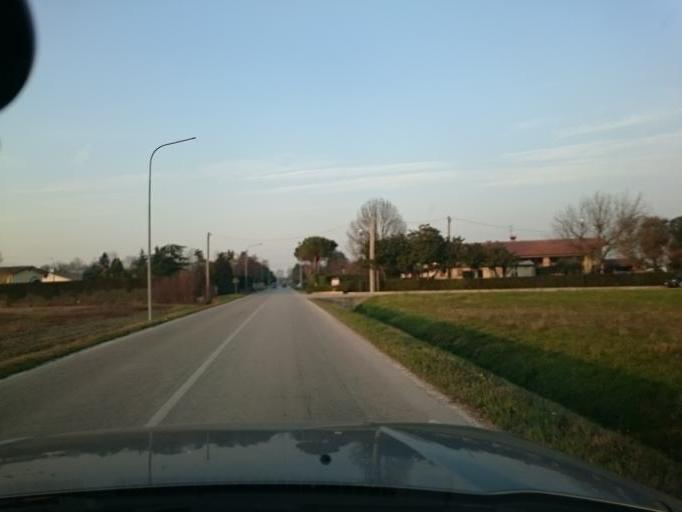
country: IT
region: Veneto
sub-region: Provincia di Padova
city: Mandriola-Sant'Agostino
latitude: 45.3620
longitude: 11.8240
